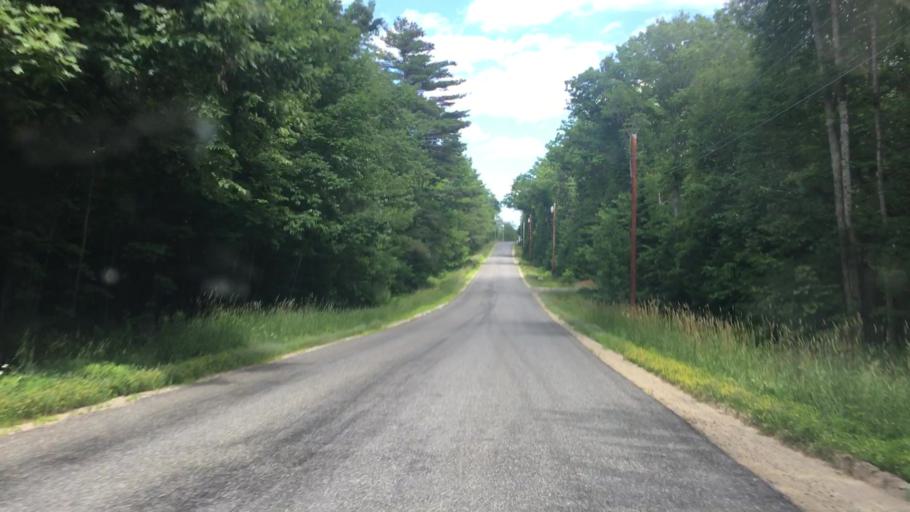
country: US
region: Maine
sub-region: Franklin County
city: Jay
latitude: 44.5361
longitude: -70.2012
